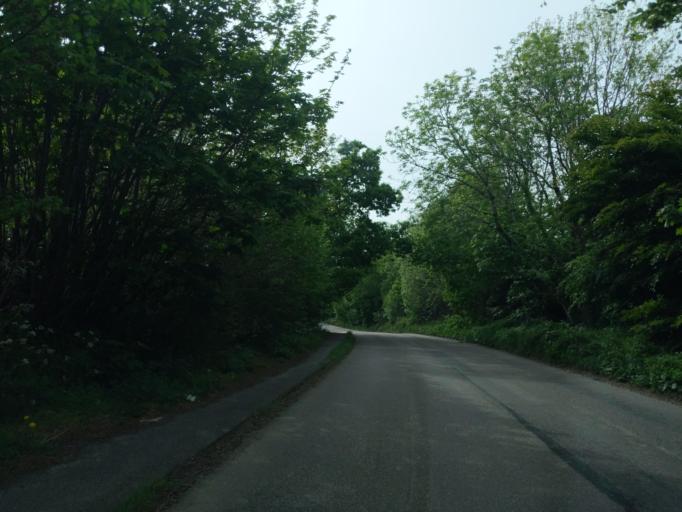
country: GB
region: England
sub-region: Devon
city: Yelverton
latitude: 50.4446
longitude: -4.0922
